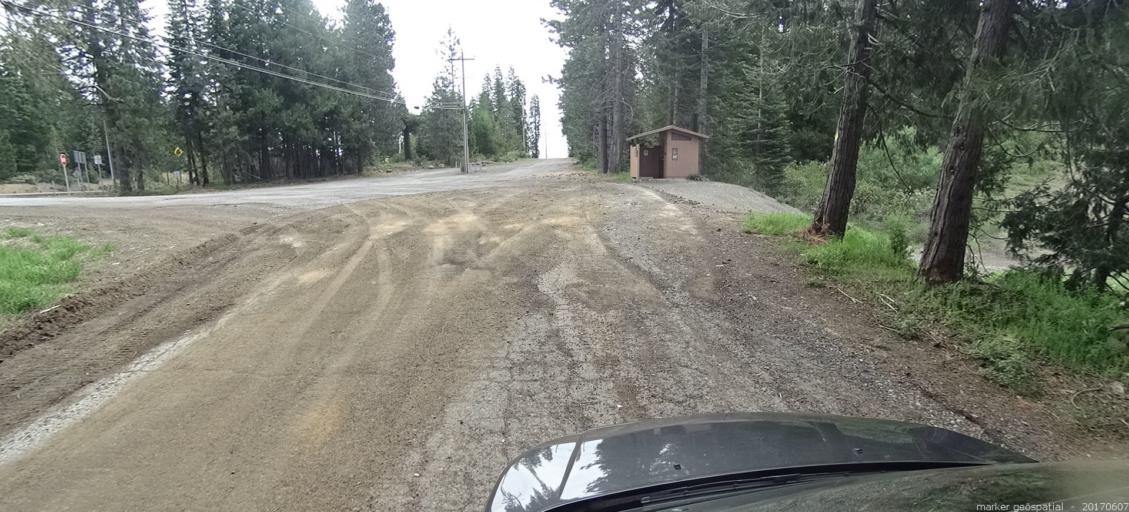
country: US
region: California
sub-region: Siskiyou County
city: McCloud
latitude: 41.2680
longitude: -122.2151
